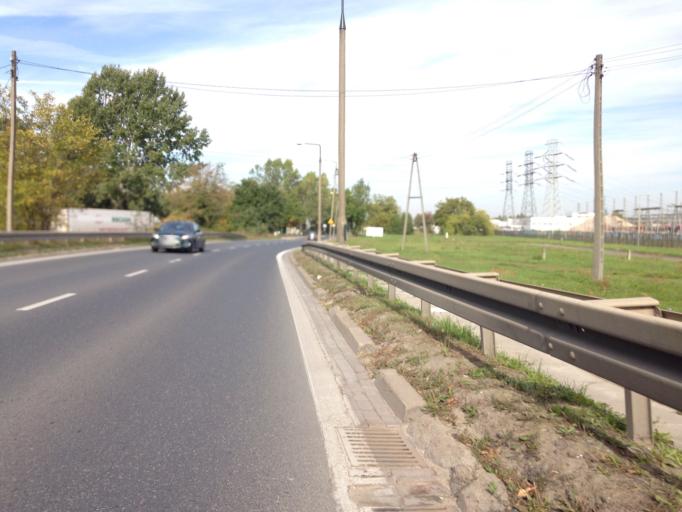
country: PL
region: Masovian Voivodeship
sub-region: Powiat wolominski
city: Zabki
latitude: 52.2632
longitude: 21.1233
